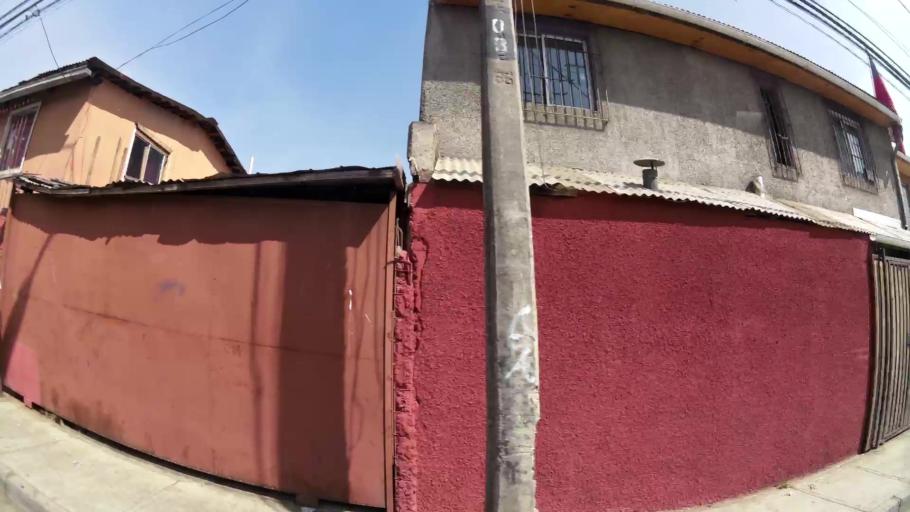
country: CL
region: Santiago Metropolitan
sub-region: Provincia de Santiago
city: Villa Presidente Frei, Nunoa, Santiago, Chile
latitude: -33.5116
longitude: -70.5802
